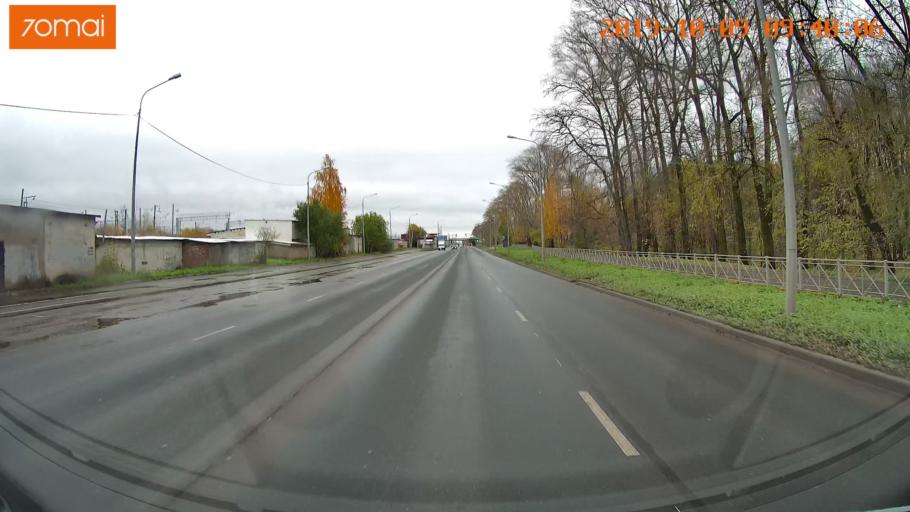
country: RU
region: Vologda
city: Vologda
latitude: 59.1965
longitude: 39.9205
